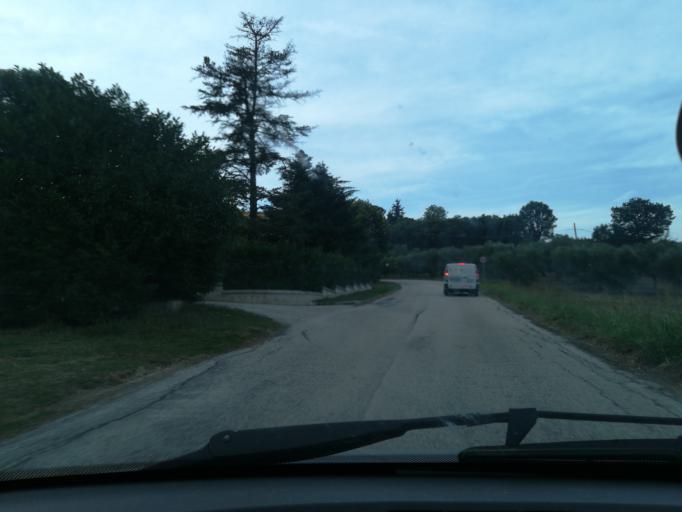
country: IT
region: The Marches
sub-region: Provincia di Macerata
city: Piediripa
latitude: 43.2935
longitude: 13.4877
